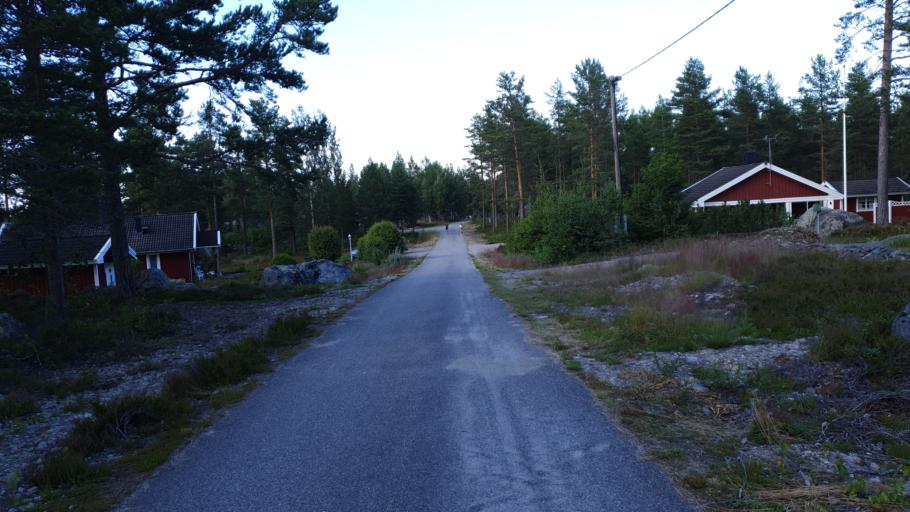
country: SE
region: Gaevleborg
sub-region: Soderhamns Kommun
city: Marielund
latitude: 61.4245
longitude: 17.1541
